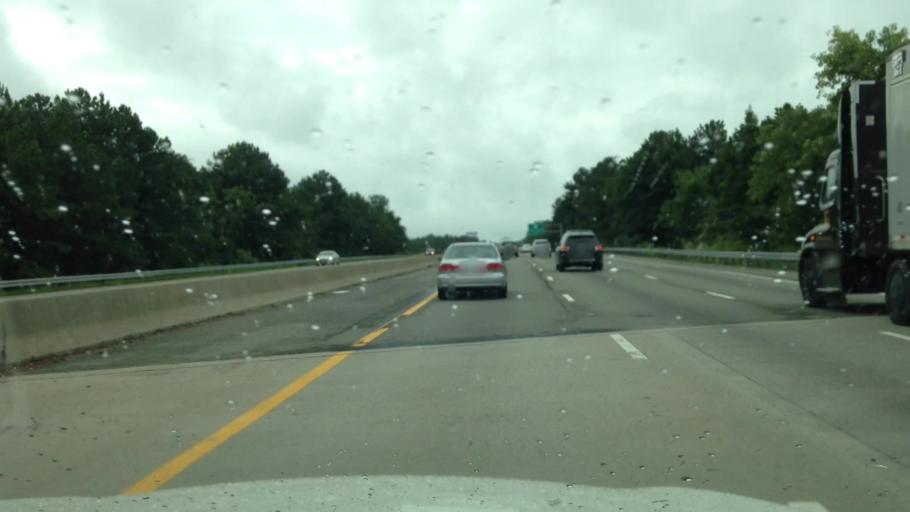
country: US
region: Virginia
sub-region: Chesterfield County
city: Bellwood
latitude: 37.4130
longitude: -77.4268
